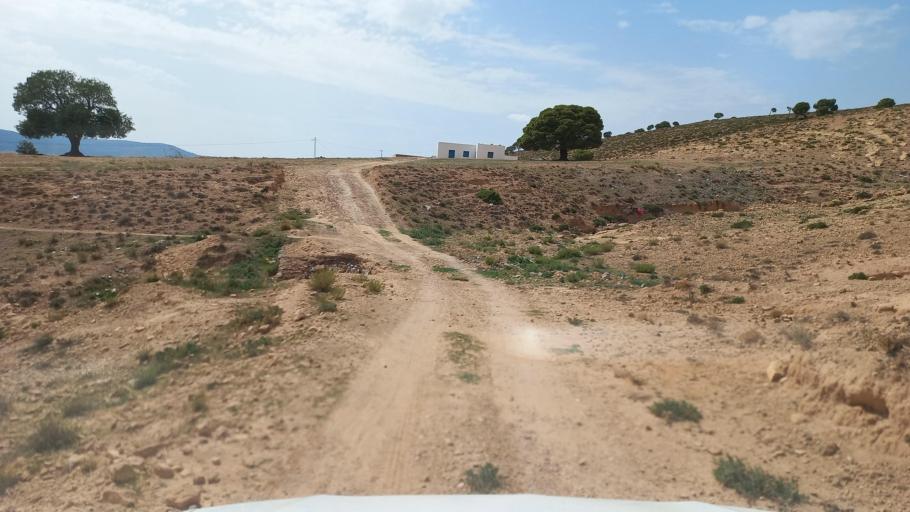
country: TN
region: Al Qasrayn
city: Kasserine
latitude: 35.3727
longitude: 8.8785
